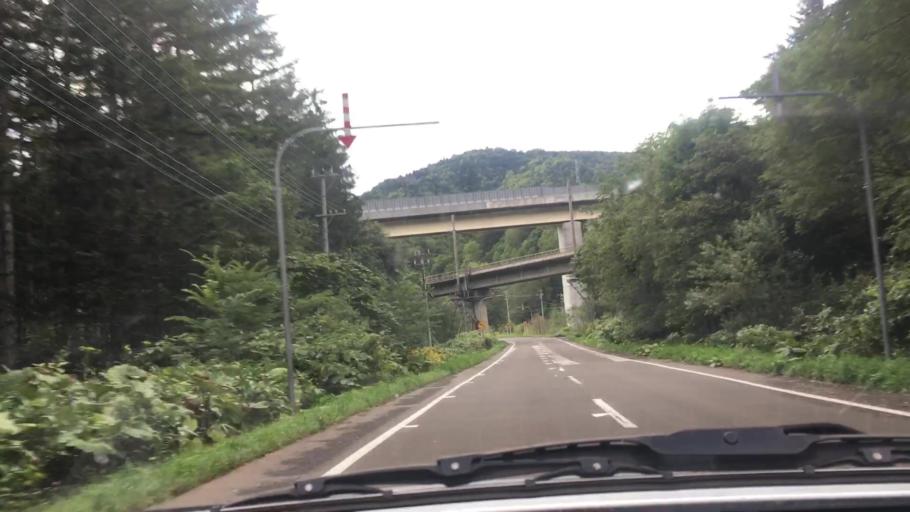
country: JP
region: Hokkaido
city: Shimo-furano
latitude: 43.0509
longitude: 142.4975
